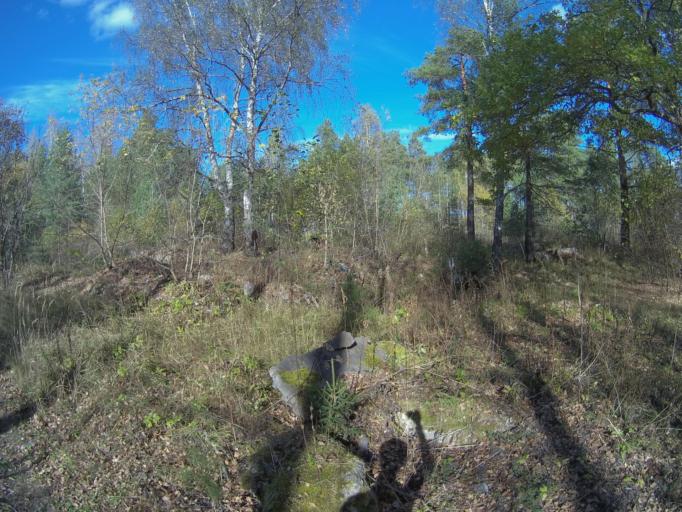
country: RU
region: Vladimir
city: Golovino
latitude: 56.0153
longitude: 40.4833
